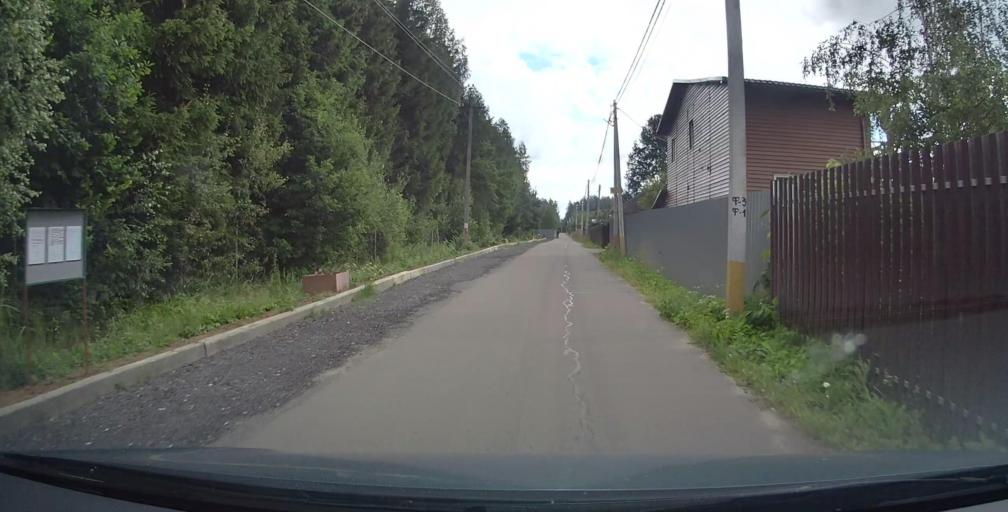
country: RU
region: Moskovskaya
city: Selyatino
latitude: 55.3939
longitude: 37.0156
